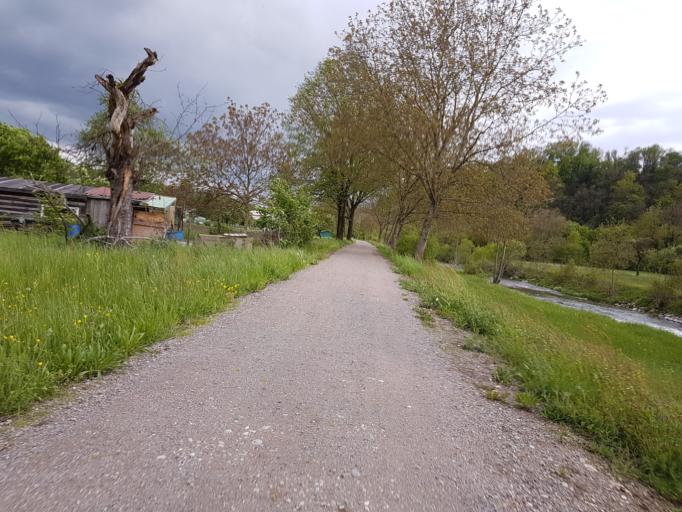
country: DE
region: Baden-Wuerttemberg
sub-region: Freiburg Region
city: Wutoschingen
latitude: 47.6723
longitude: 8.3779
